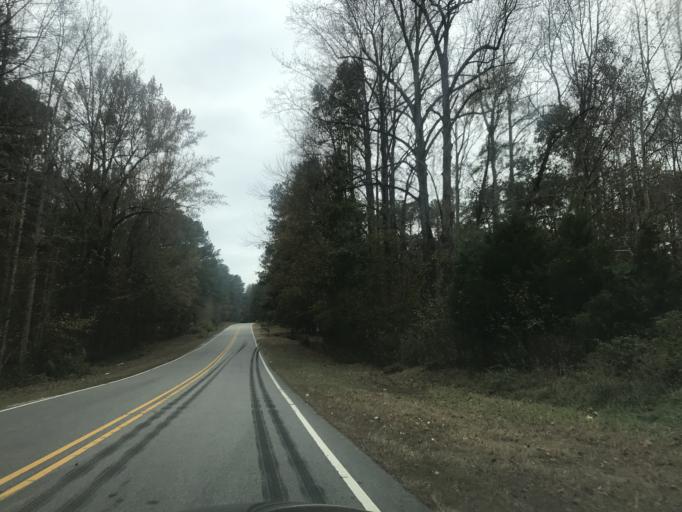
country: US
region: North Carolina
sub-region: Wake County
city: Wake Forest
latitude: 36.0006
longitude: -78.4953
